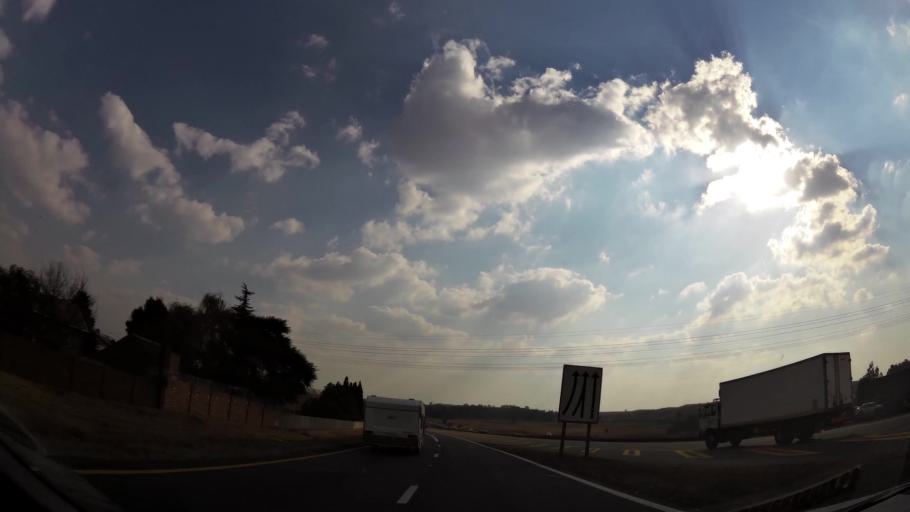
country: ZA
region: Gauteng
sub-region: Ekurhuleni Metropolitan Municipality
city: Boksburg
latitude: -26.2517
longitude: 28.2379
